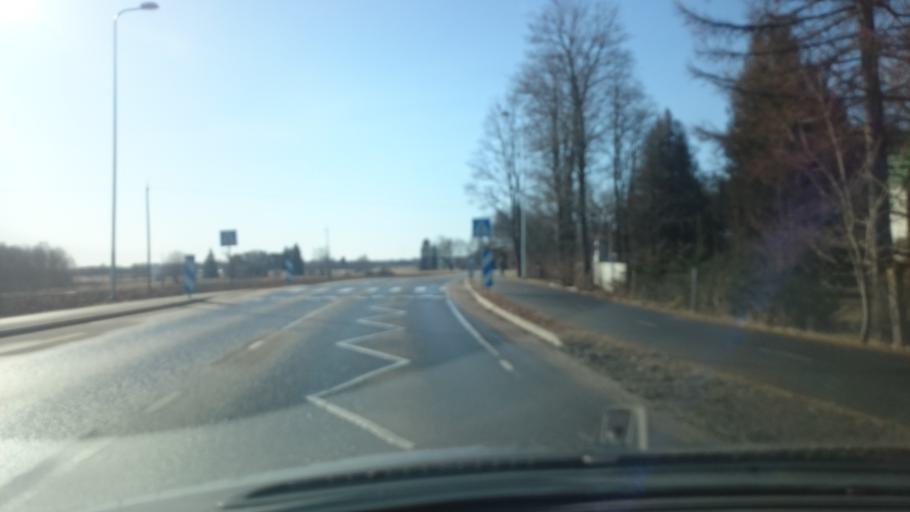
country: EE
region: Harju
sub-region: Saku vald
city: Saku
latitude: 59.2759
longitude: 24.7192
